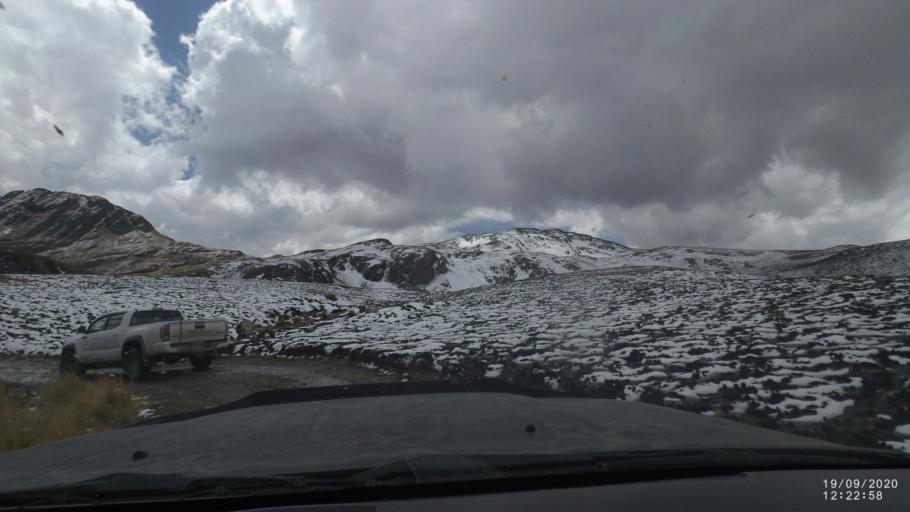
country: BO
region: Cochabamba
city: Cochabamba
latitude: -17.2959
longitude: -66.1085
